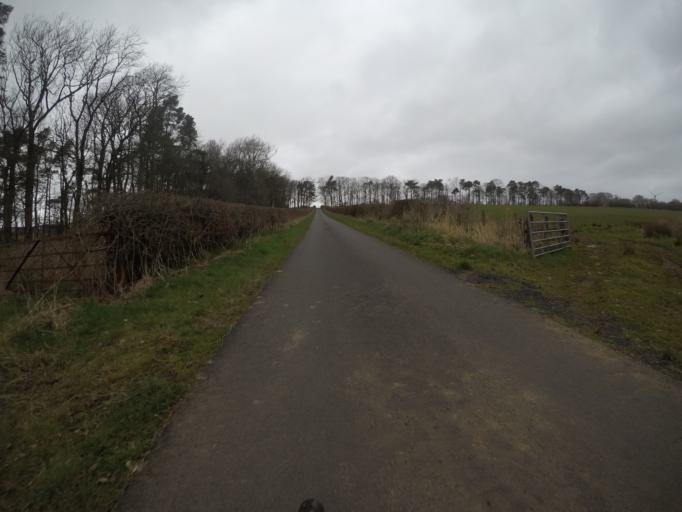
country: GB
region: Scotland
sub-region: East Ayrshire
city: Galston
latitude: 55.6223
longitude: -4.3557
